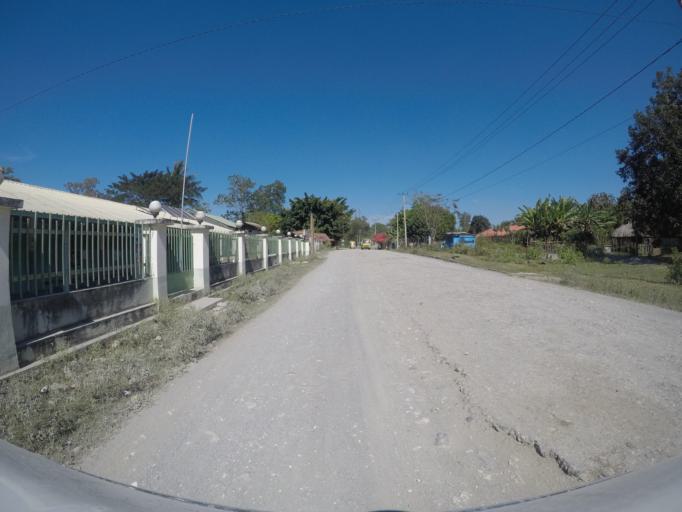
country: TL
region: Viqueque
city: Viqueque
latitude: -8.9767
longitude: 126.0438
